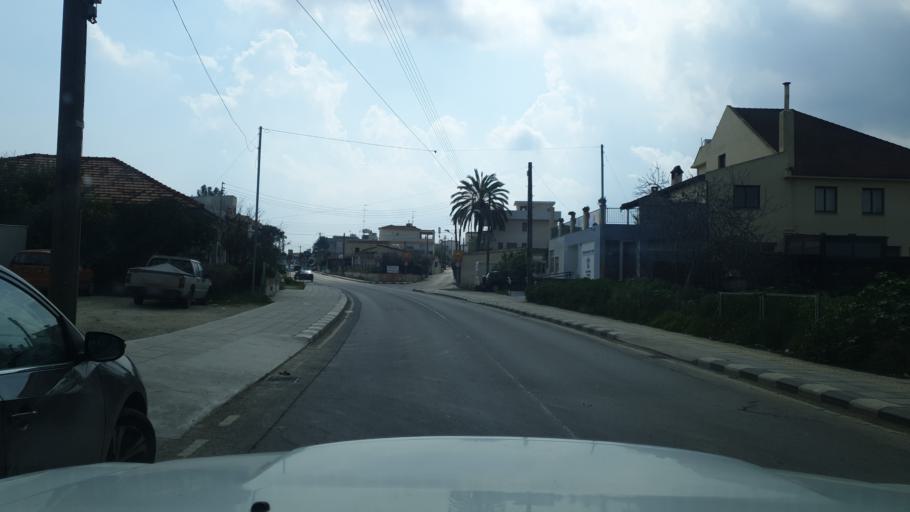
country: CY
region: Lefkosia
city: Tseri
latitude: 35.0755
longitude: 33.3242
